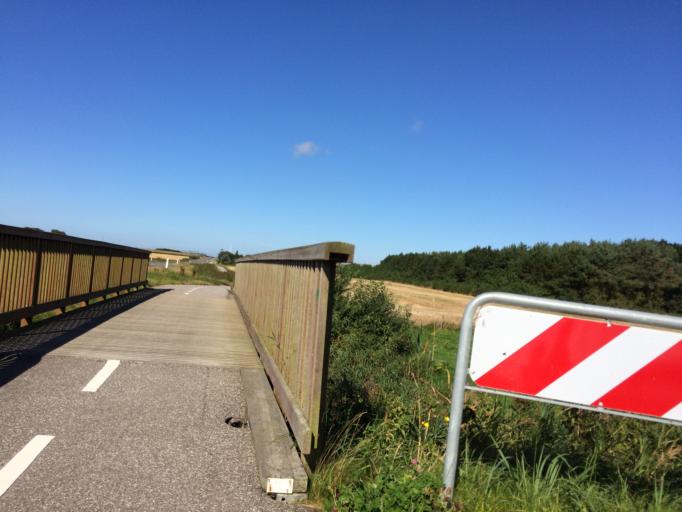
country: DK
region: Central Jutland
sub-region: Holstebro Kommune
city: Ulfborg
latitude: 56.2722
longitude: 8.2128
